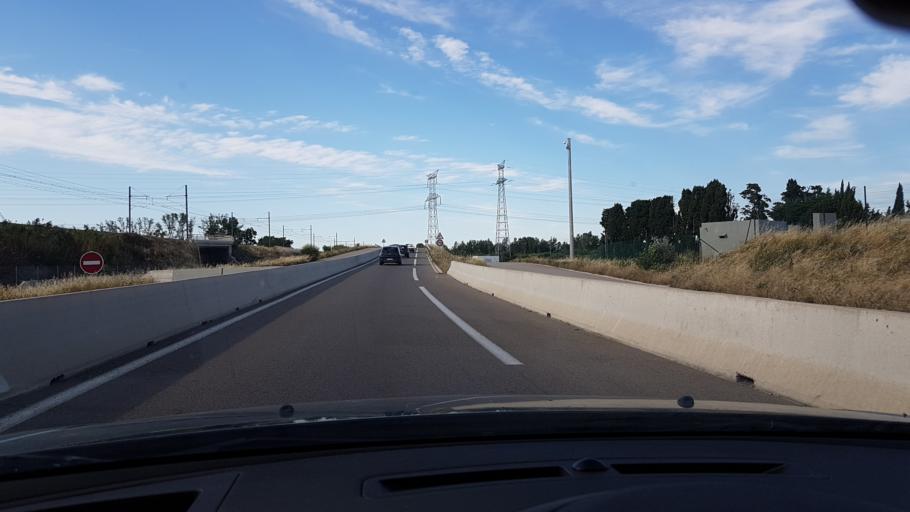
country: FR
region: Provence-Alpes-Cote d'Azur
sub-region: Departement des Bouches-du-Rhone
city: Rognonas
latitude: 43.9113
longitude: 4.7921
